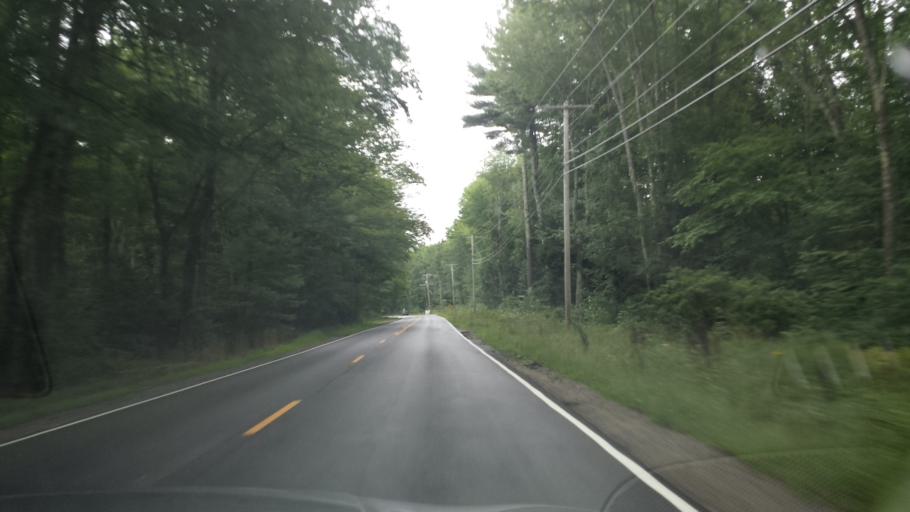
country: US
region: Maine
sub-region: York County
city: South Sanford
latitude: 43.4006
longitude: -70.6798
